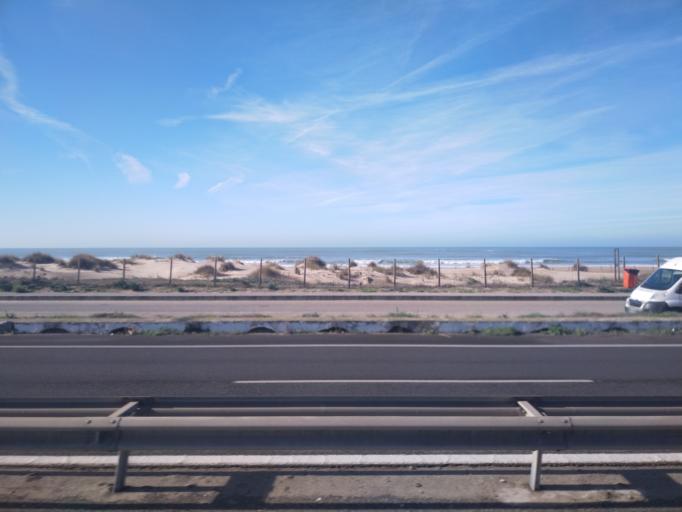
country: ES
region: Andalusia
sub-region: Provincia de Cadiz
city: Cadiz
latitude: 36.4922
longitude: -6.2688
